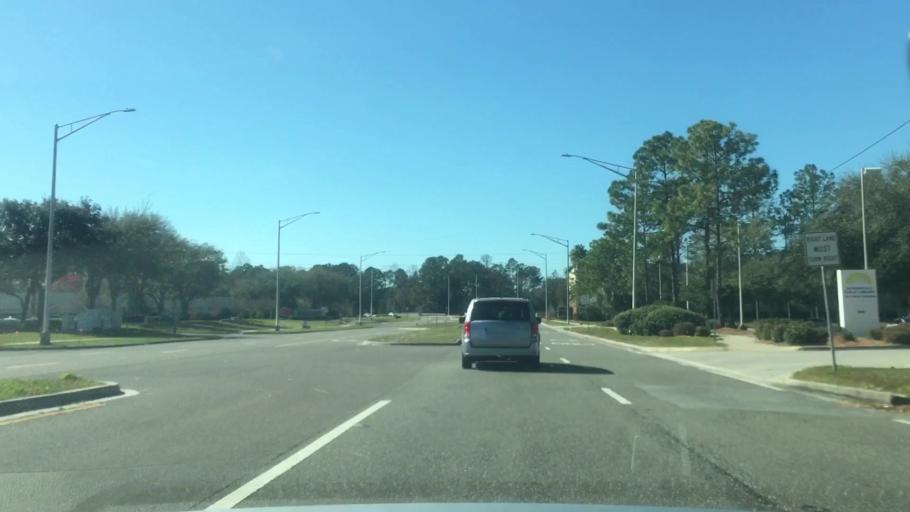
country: US
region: Florida
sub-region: Duval County
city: Jacksonville
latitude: 30.2477
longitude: -81.5391
